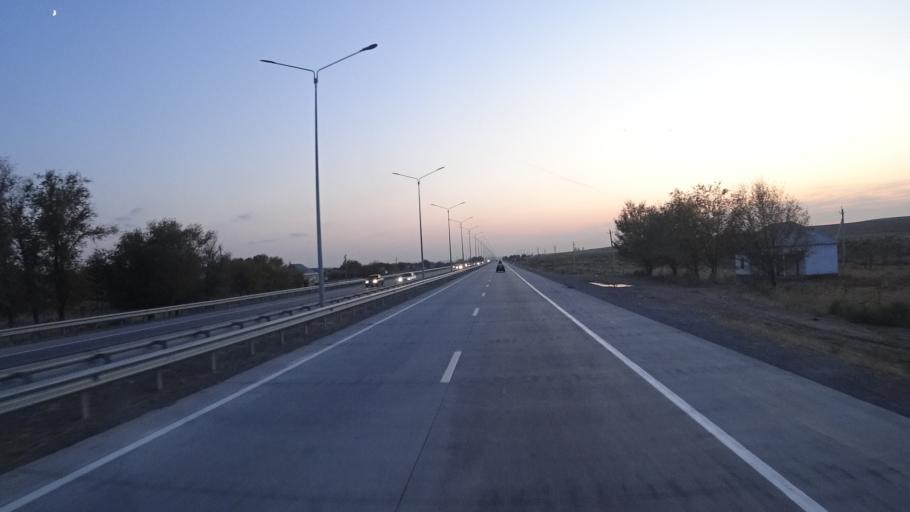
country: KZ
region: Ongtustik Qazaqstan
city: Qazyqurt
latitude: 41.8916
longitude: 69.4483
